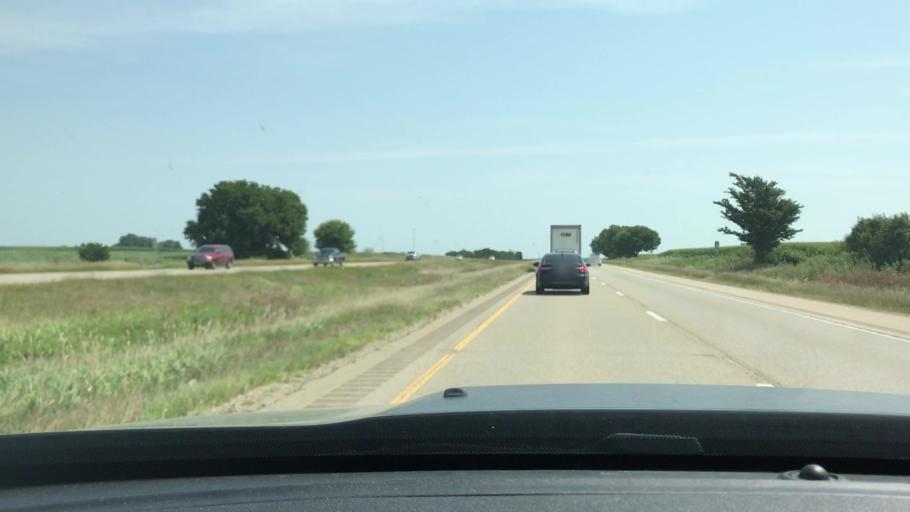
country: US
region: Illinois
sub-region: Bureau County
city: Princeton
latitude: 41.3978
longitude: -89.4220
